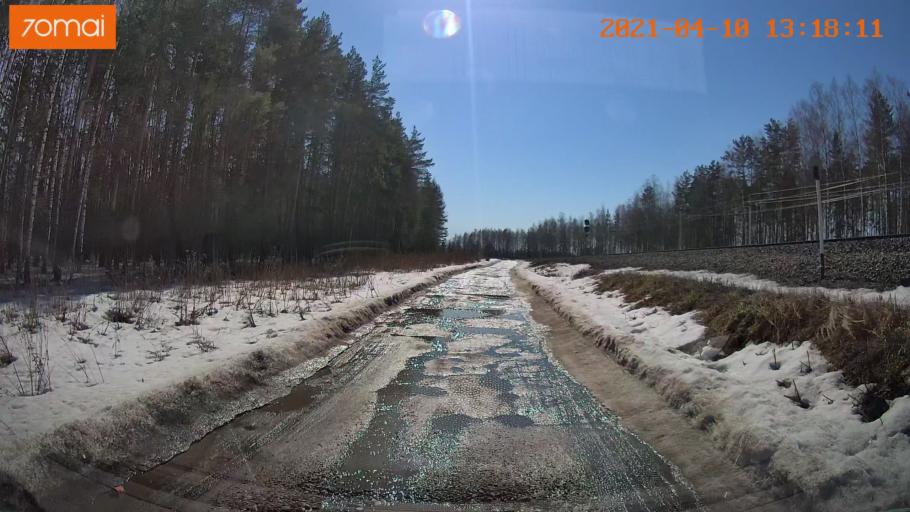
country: RU
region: Ivanovo
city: Kokhma
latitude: 56.9936
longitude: 41.0581
